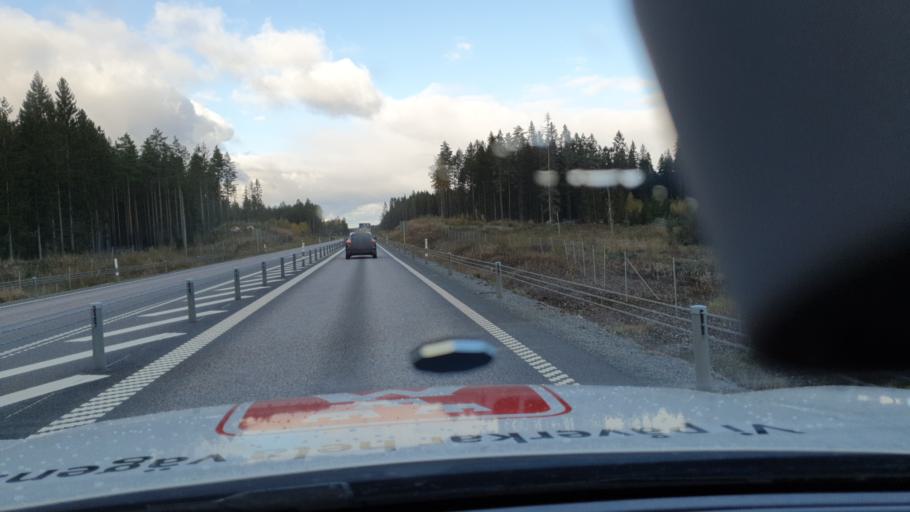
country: SE
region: Uppsala
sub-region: Heby Kommun
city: Tarnsjo
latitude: 60.1023
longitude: 16.9205
